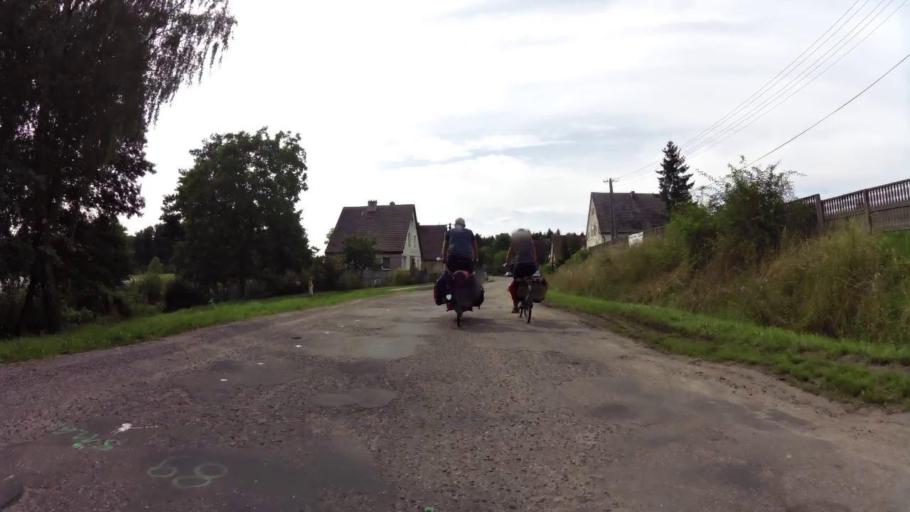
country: PL
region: West Pomeranian Voivodeship
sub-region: Powiat lobeski
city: Wegorzyno
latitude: 53.5416
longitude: 15.5670
